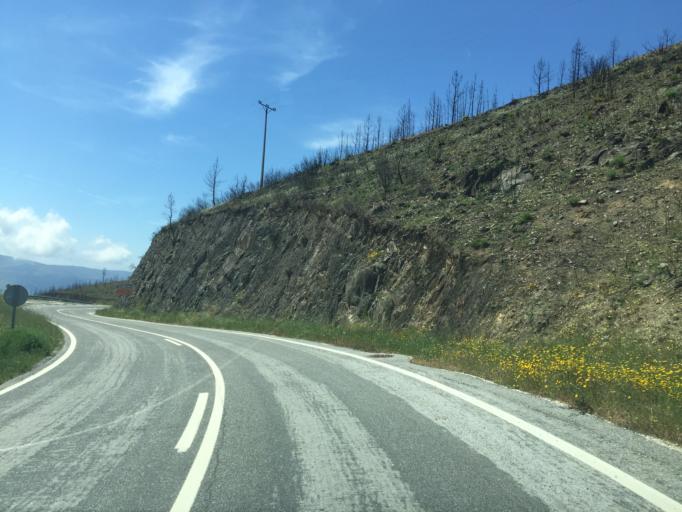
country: PT
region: Coimbra
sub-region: Pampilhosa da Serra
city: Pampilhosa da Serra
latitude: 40.0191
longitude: -7.9656
